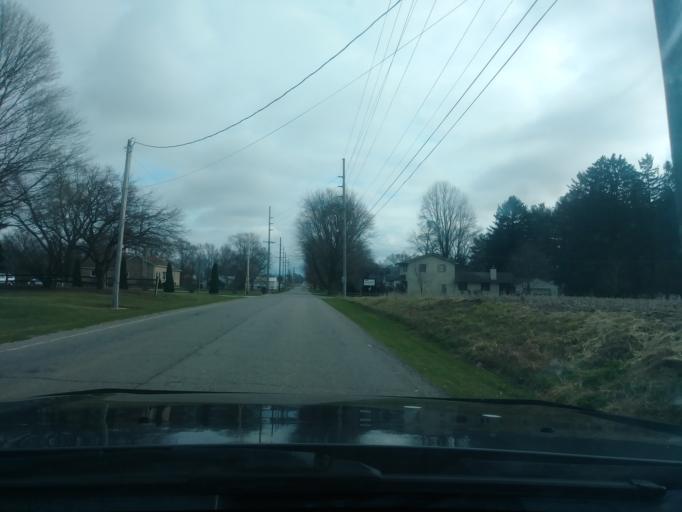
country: US
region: Indiana
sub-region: LaPorte County
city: LaPorte
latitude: 41.5997
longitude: -86.7979
